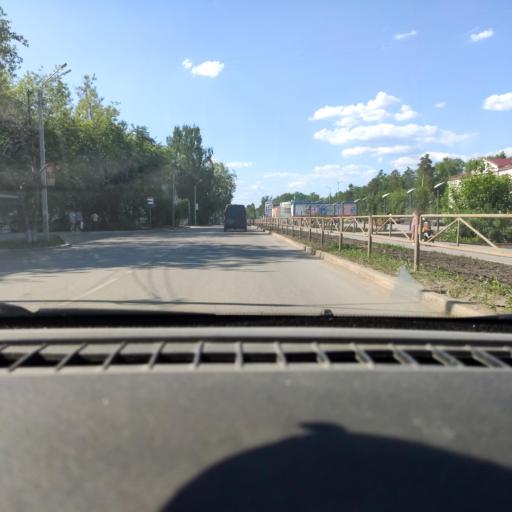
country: RU
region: Perm
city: Krasnokamsk
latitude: 58.0809
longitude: 55.7586
